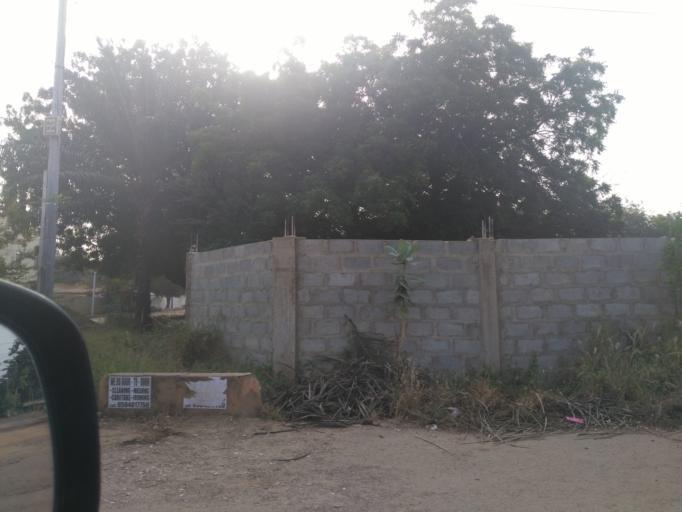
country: GH
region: Greater Accra
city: Accra
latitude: 5.6051
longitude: -0.2024
